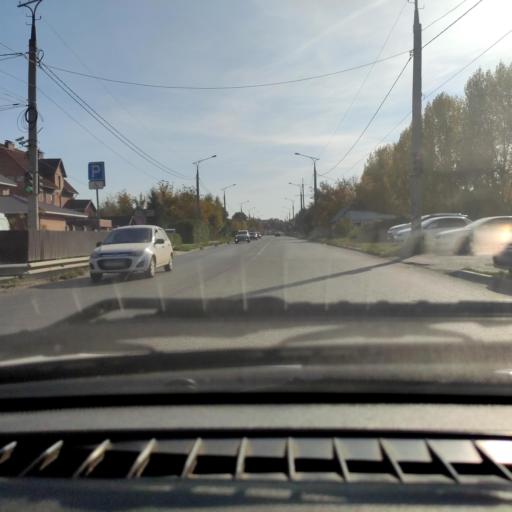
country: RU
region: Samara
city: Tol'yatti
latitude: 53.5132
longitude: 49.3953
